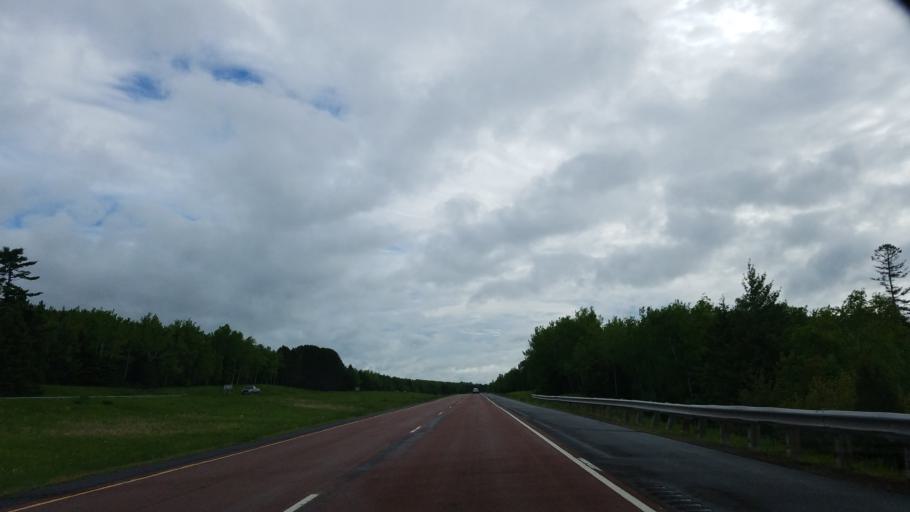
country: US
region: Minnesota
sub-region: Saint Louis County
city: Arnold
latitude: 46.9014
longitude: -91.8990
